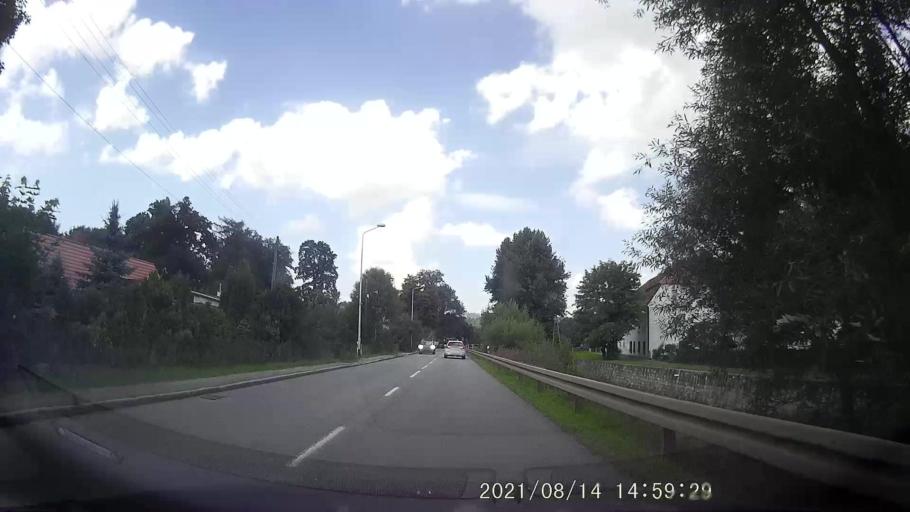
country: PL
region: Lower Silesian Voivodeship
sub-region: Powiat walbrzyski
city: Jedlina-Zdroj
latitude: 50.7106
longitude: 16.3616
